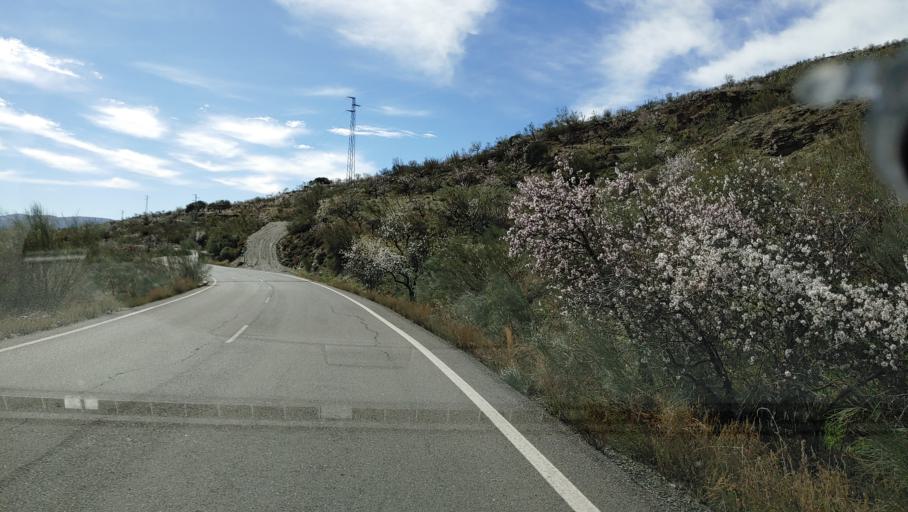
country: ES
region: Andalusia
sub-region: Provincia de Almeria
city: Ohanes
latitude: 37.0465
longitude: -2.7324
